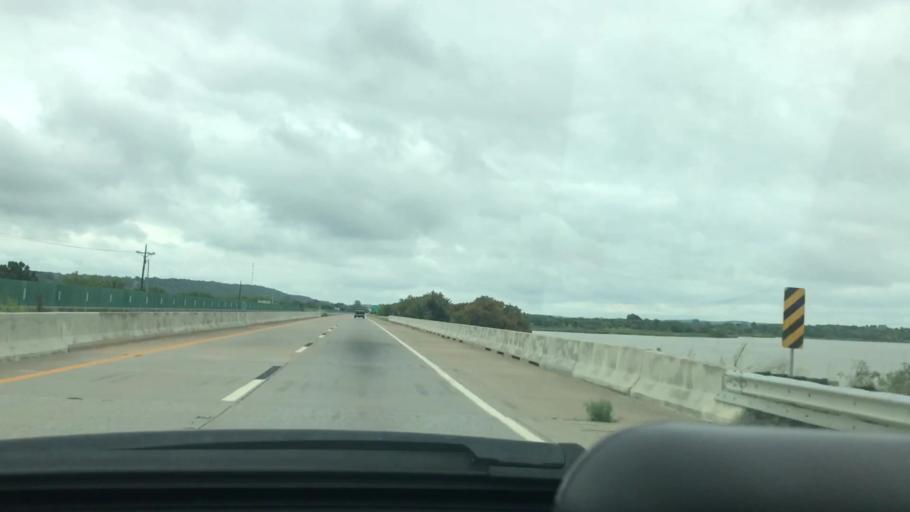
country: US
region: Oklahoma
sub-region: Pittsburg County
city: Krebs
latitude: 35.0437
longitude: -95.7107
